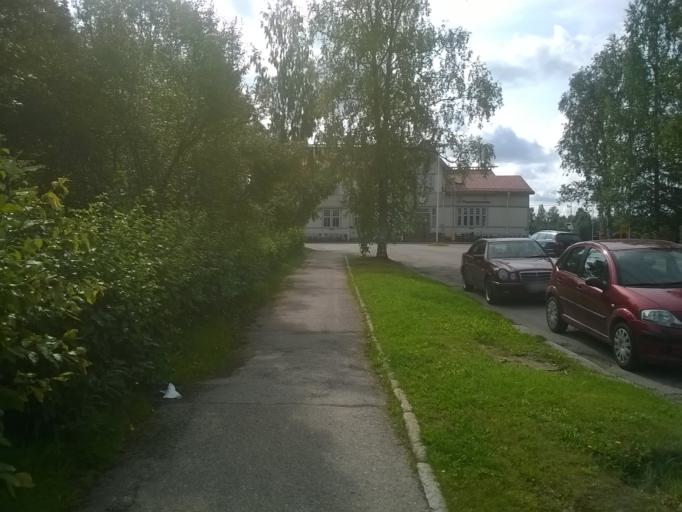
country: FI
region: Kainuu
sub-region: Kajaani
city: Kajaani
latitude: 64.2207
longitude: 27.7385
